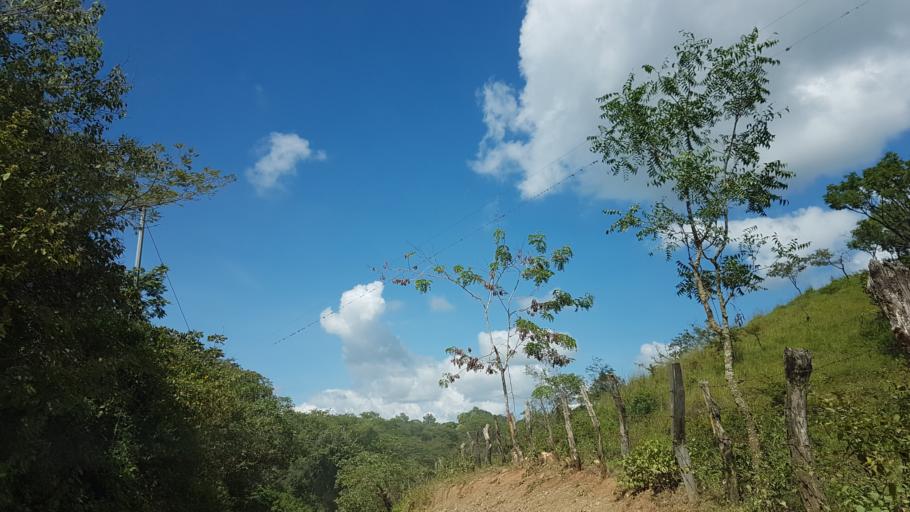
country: HN
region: El Paraiso
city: Oropoli
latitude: 13.7424
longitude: -86.7060
